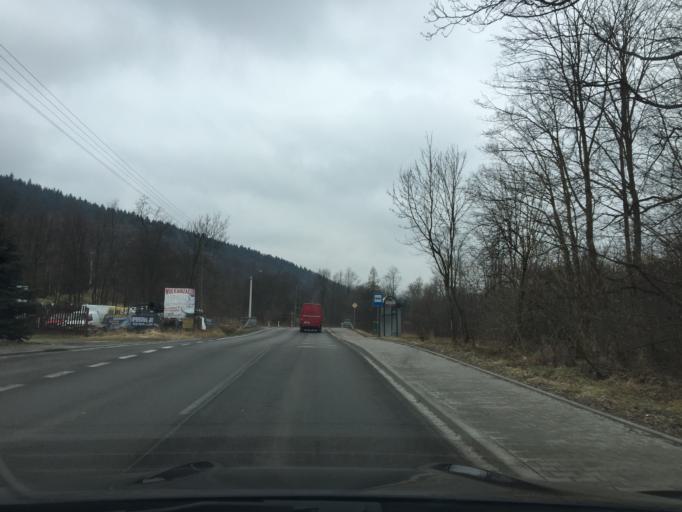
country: PL
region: Lesser Poland Voivodeship
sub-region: Powiat suski
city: Palcza
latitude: 49.7983
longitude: 19.7325
